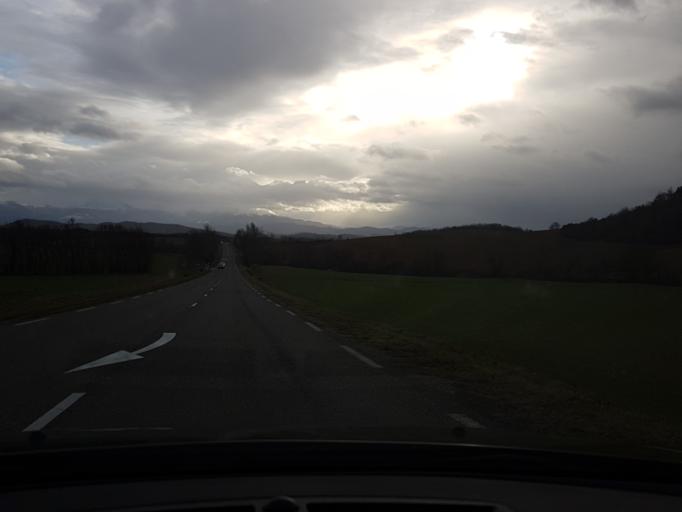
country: FR
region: Midi-Pyrenees
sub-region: Departement de l'Ariege
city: Mirepoix
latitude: 43.1208
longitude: 1.9346
